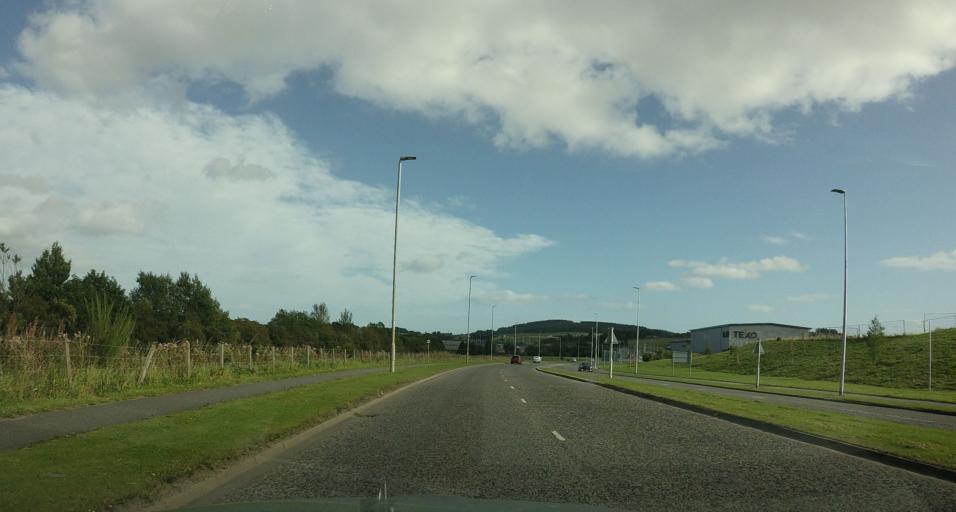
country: GB
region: Scotland
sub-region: Aberdeenshire
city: Westhill
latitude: 57.1502
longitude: -2.2718
